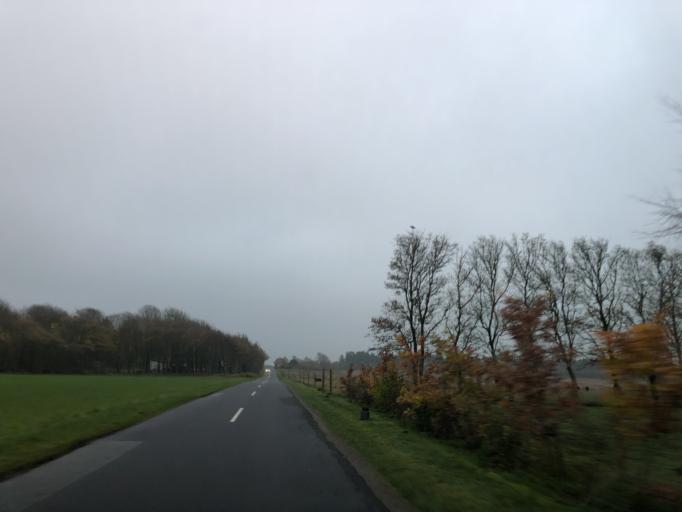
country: DK
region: Central Jutland
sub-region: Ringkobing-Skjern Kommune
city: Videbaek
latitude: 56.1903
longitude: 8.6422
